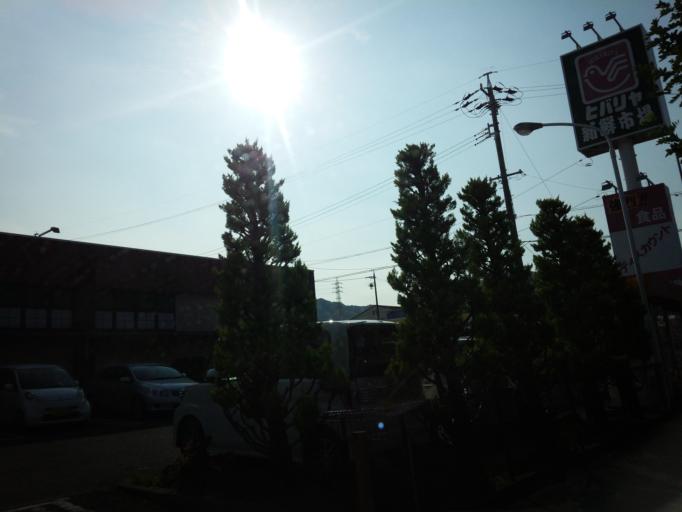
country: JP
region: Shizuoka
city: Shizuoka-shi
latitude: 35.0350
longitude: 138.4573
